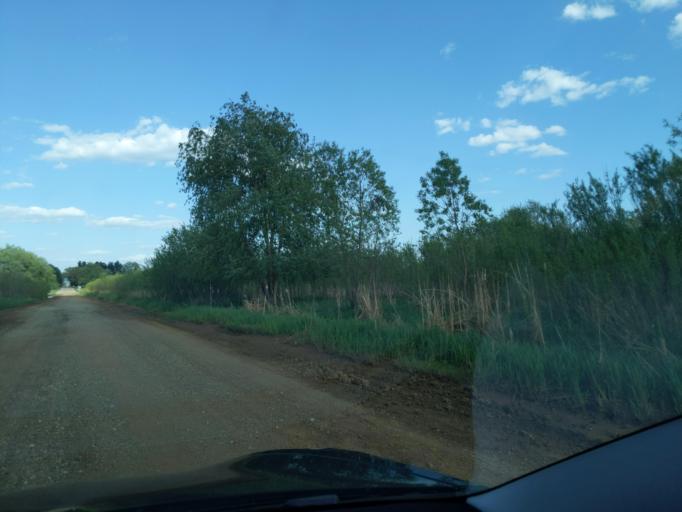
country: US
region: Michigan
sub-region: Eaton County
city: Potterville
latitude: 42.6829
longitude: -84.7233
